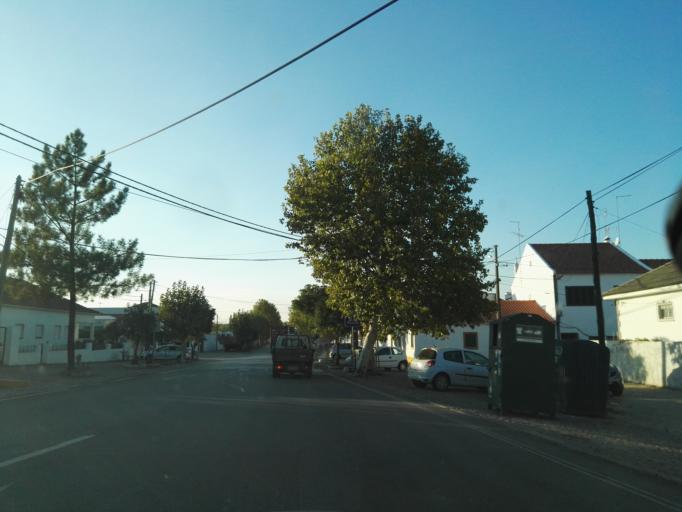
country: PT
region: Evora
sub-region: Arraiolos
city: Arraiolos
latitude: 38.8296
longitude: -7.8402
